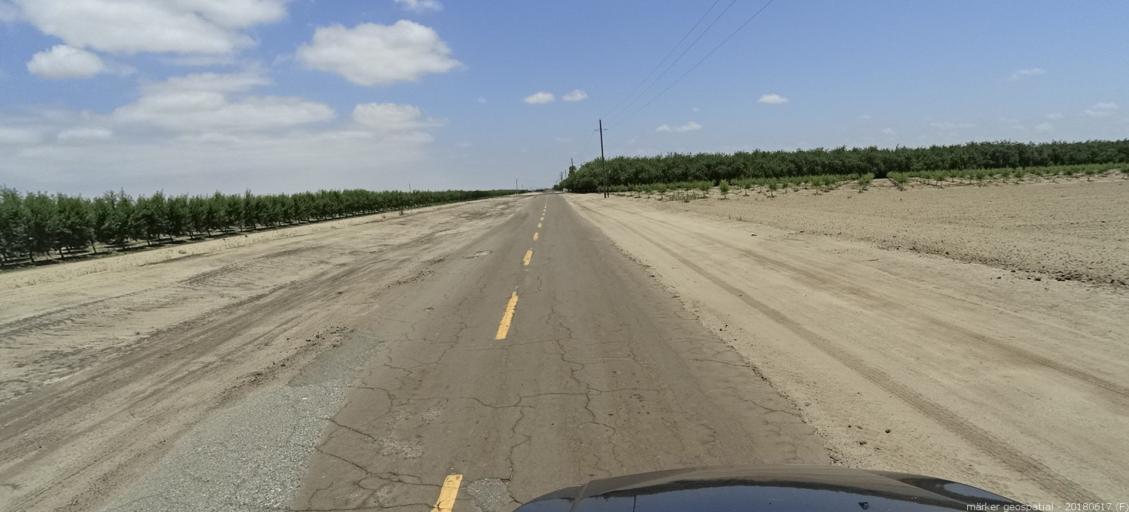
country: US
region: California
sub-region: Fresno County
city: Biola
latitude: 36.8222
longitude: -120.1409
